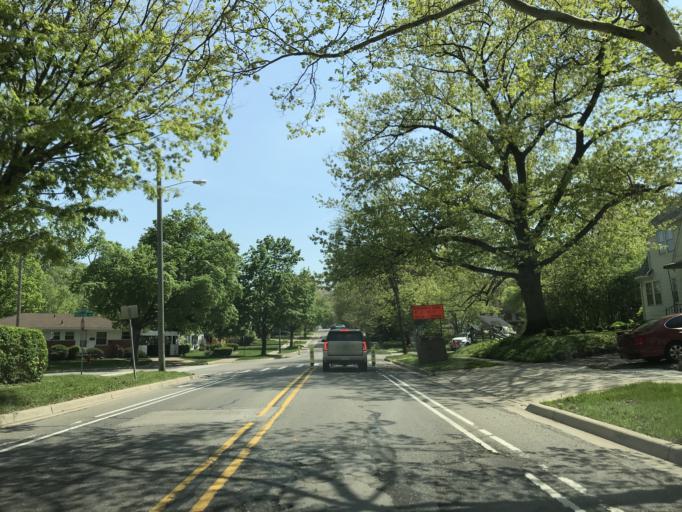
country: US
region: Michigan
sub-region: Washtenaw County
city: Ann Arbor
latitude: 42.2660
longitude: -83.7582
